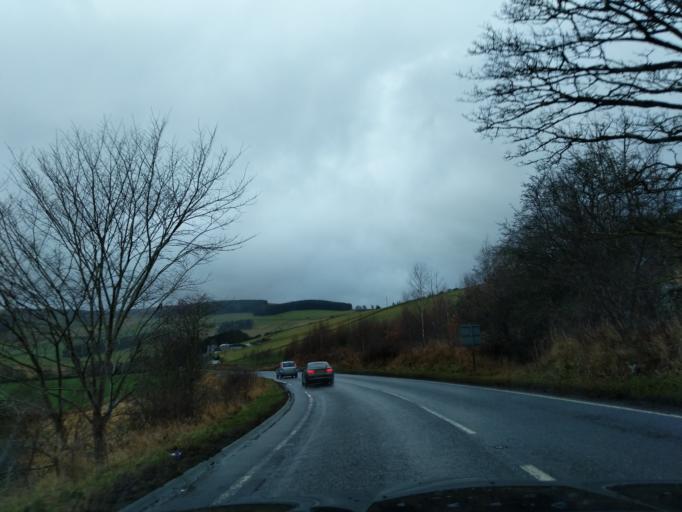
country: GB
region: Scotland
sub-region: The Scottish Borders
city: Galashiels
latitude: 55.6645
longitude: -2.8645
